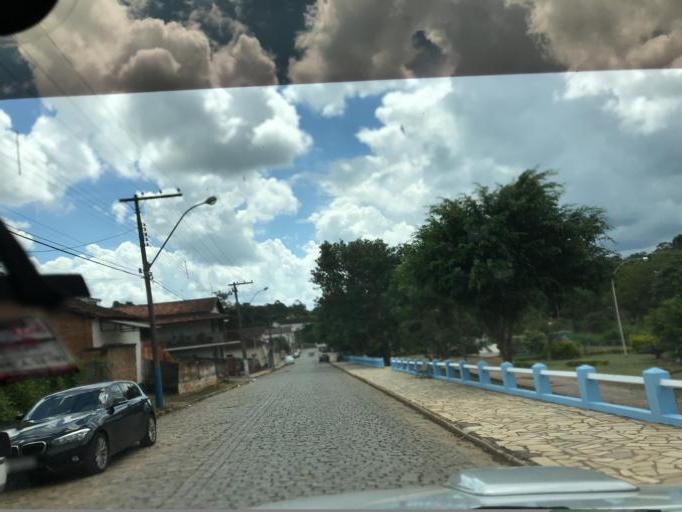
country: BR
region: Minas Gerais
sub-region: Cambuquira
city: Cambuquira
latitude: -21.8501
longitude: -45.2950
